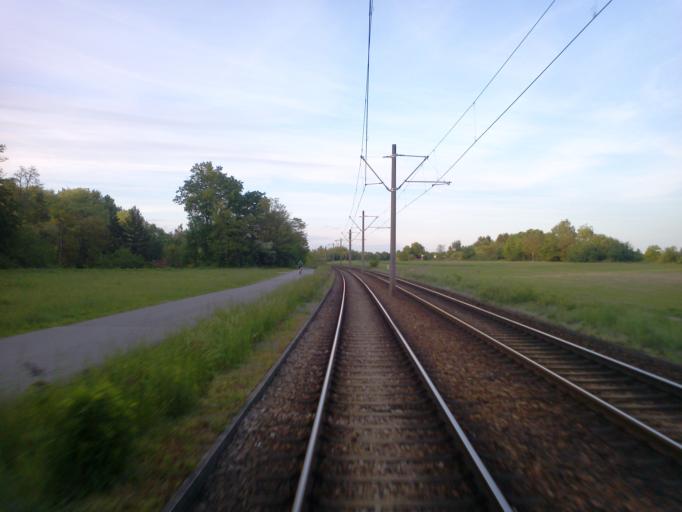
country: DE
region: Baden-Wuerttemberg
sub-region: Karlsruhe Region
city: Rheinstetten
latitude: 48.9854
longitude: 8.3283
